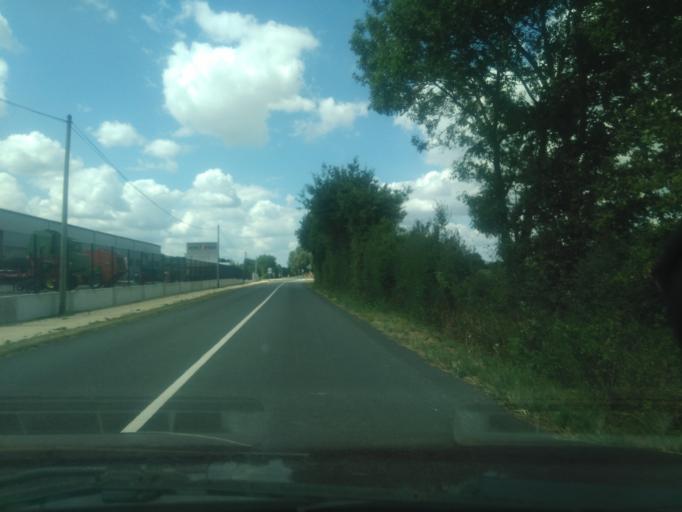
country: FR
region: Pays de la Loire
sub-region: Departement de la Vendee
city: Chauche
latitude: 46.8363
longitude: -1.2820
